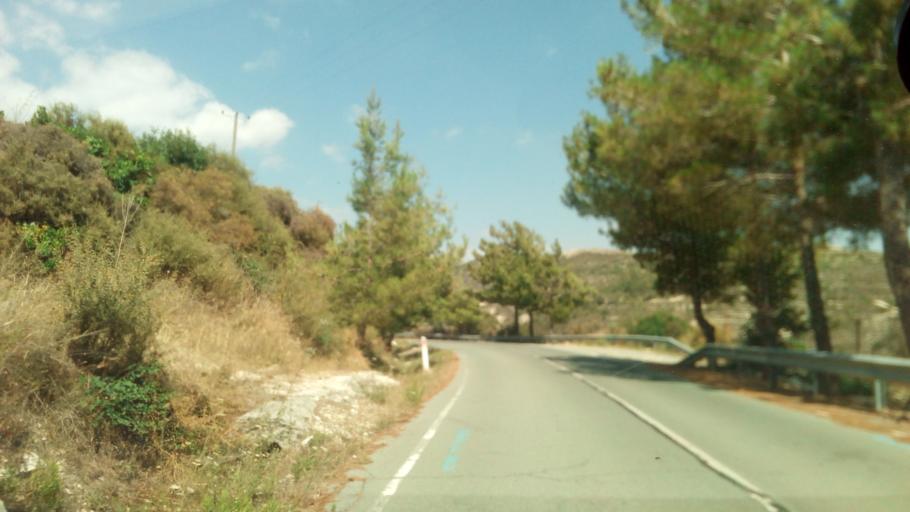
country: CY
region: Limassol
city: Pachna
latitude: 34.8345
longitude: 32.8554
